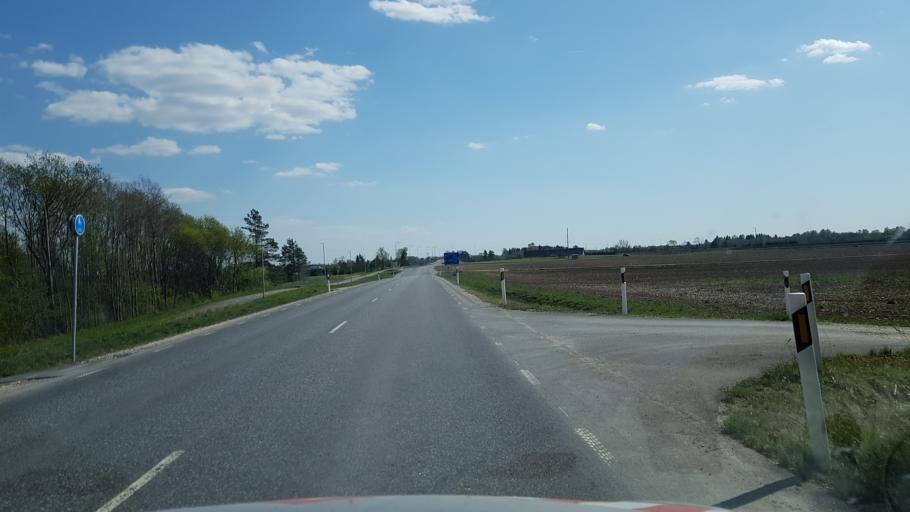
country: EE
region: Harju
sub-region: Raasiku vald
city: Arukula
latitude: 59.1886
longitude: 25.1141
